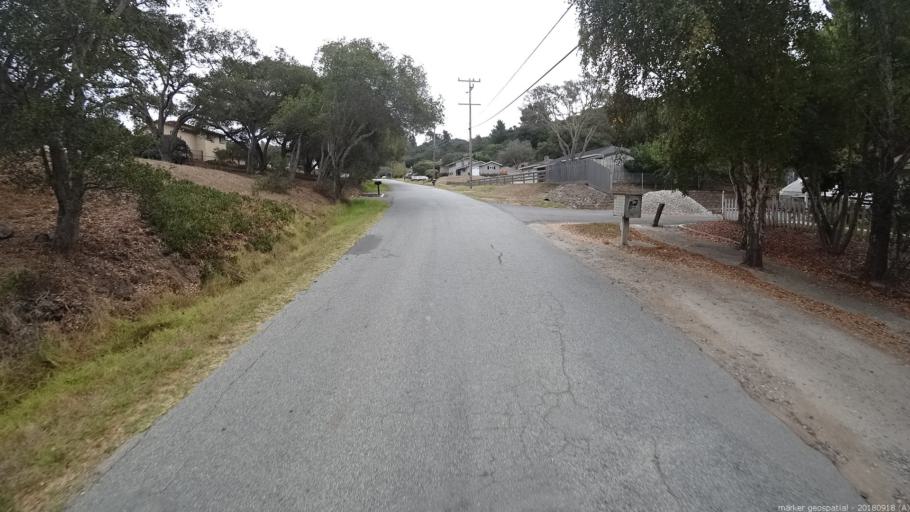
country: US
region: California
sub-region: Monterey County
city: Prunedale
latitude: 36.7908
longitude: -121.6554
